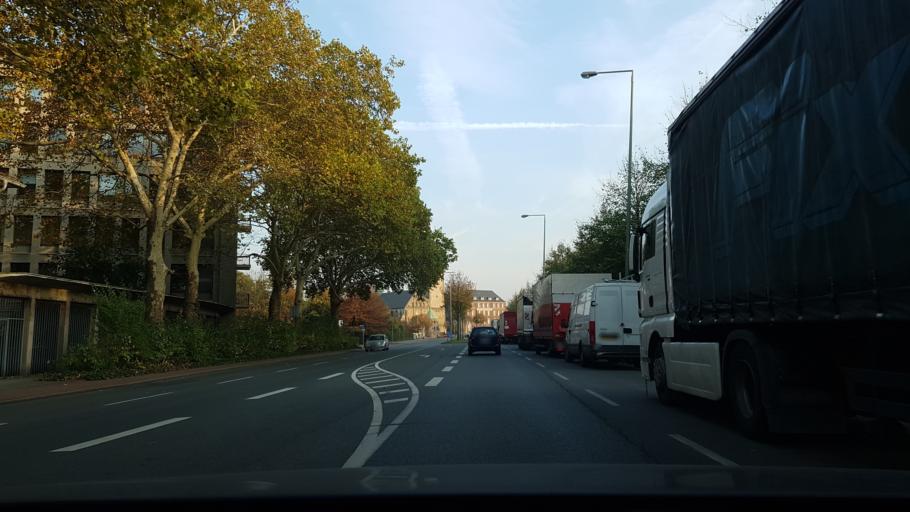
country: DE
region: North Rhine-Westphalia
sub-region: Regierungsbezirk Dusseldorf
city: Hochfeld
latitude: 51.4160
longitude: 6.7494
